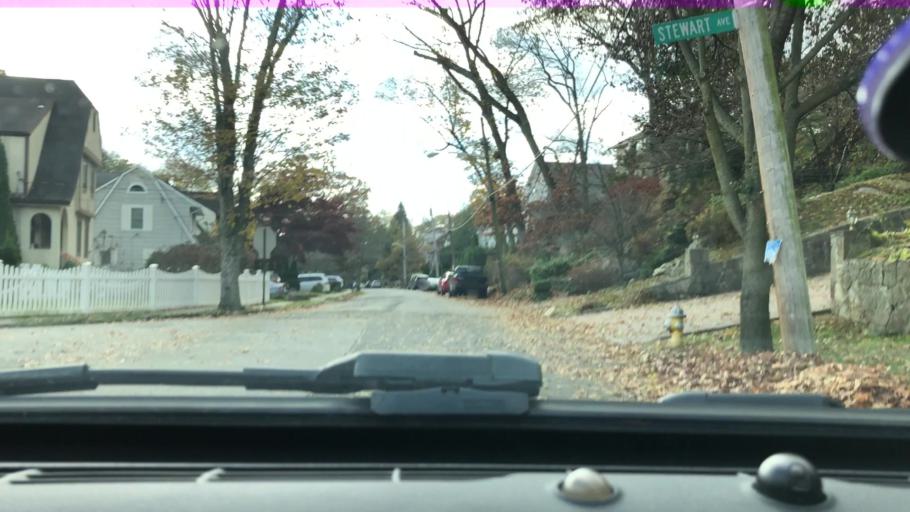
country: US
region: New York
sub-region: Westchester County
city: Tuckahoe
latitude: 40.9622
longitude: -73.8157
